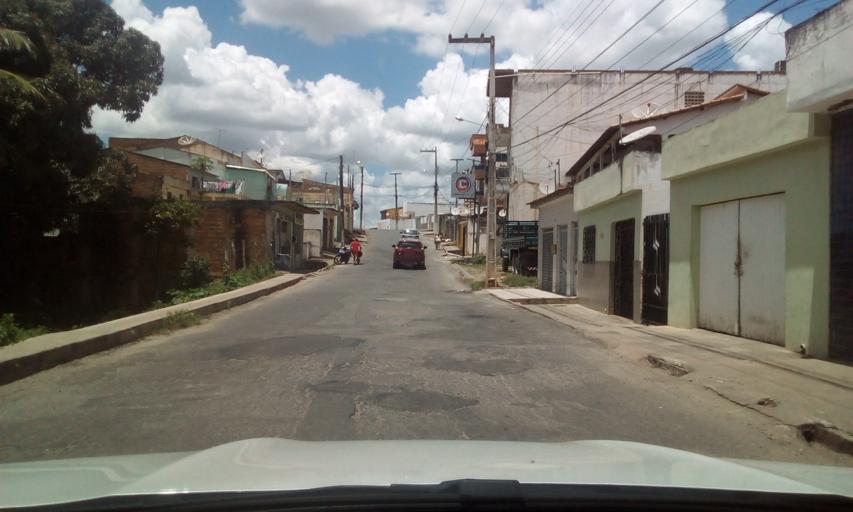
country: BR
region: Paraiba
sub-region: Guarabira
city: Guarabira
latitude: -6.8546
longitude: -35.4828
